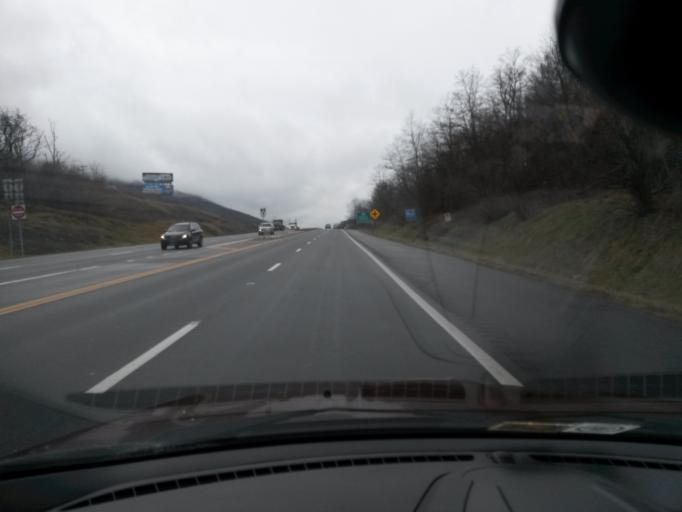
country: US
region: West Virginia
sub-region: Mercer County
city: Princeton
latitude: 37.2834
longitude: -81.1291
